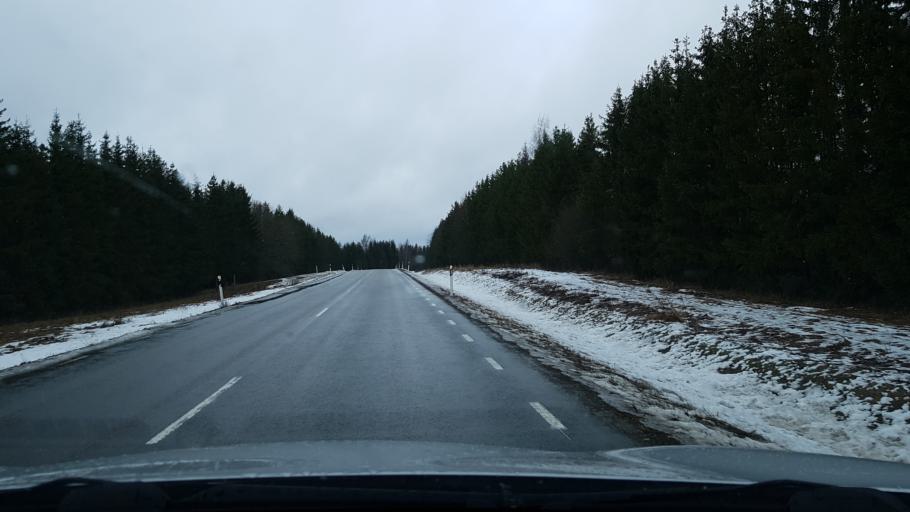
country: LV
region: Apes Novads
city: Ape
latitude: 57.5937
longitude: 26.6289
